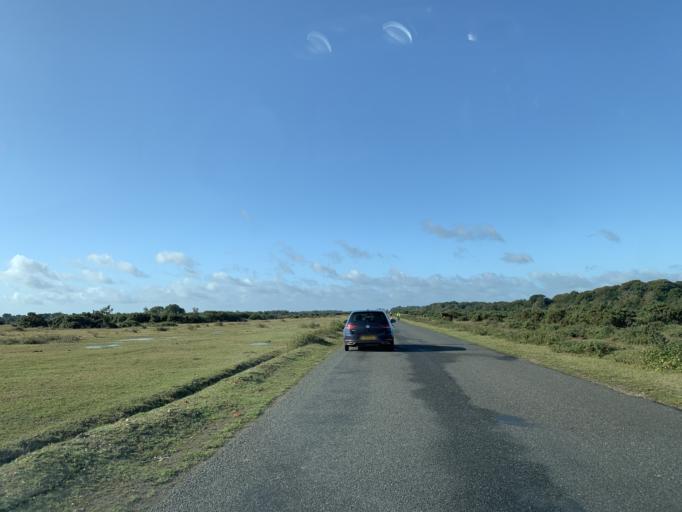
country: GB
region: England
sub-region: Hampshire
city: Cadnam
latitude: 50.9138
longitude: -1.6587
